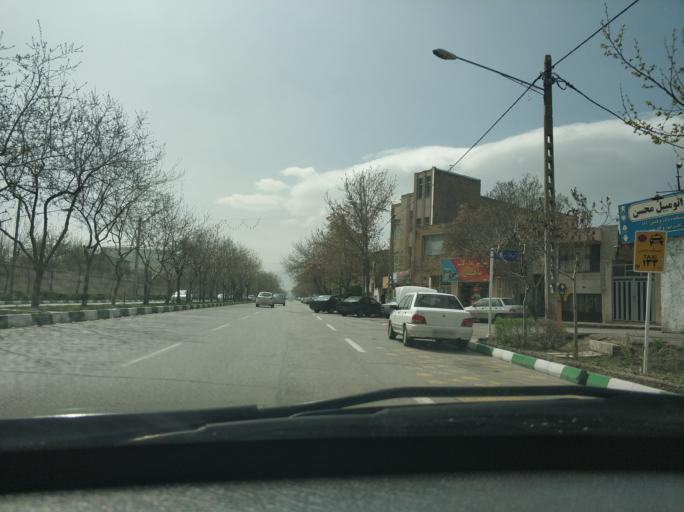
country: IR
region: Razavi Khorasan
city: Mashhad
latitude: 36.2800
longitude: 59.5771
